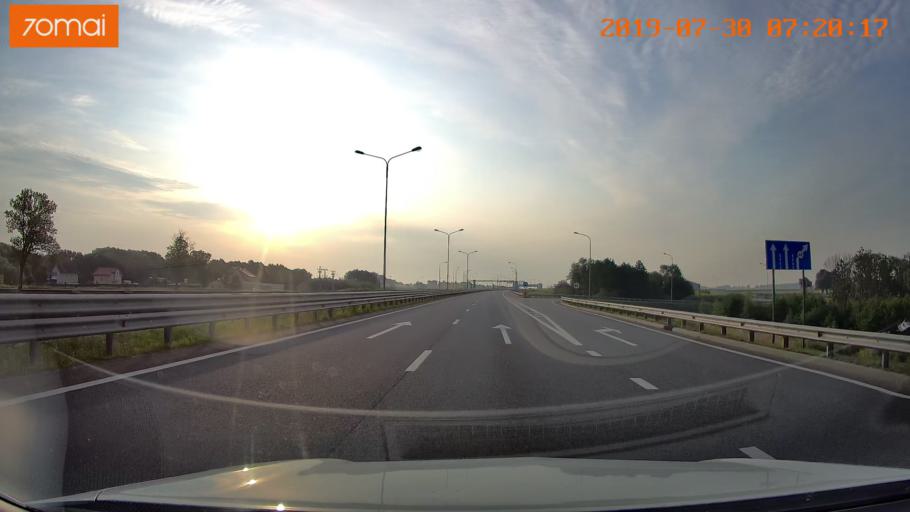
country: RU
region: Kaliningrad
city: Bol'shoe Isakovo
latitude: 54.7008
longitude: 20.6985
